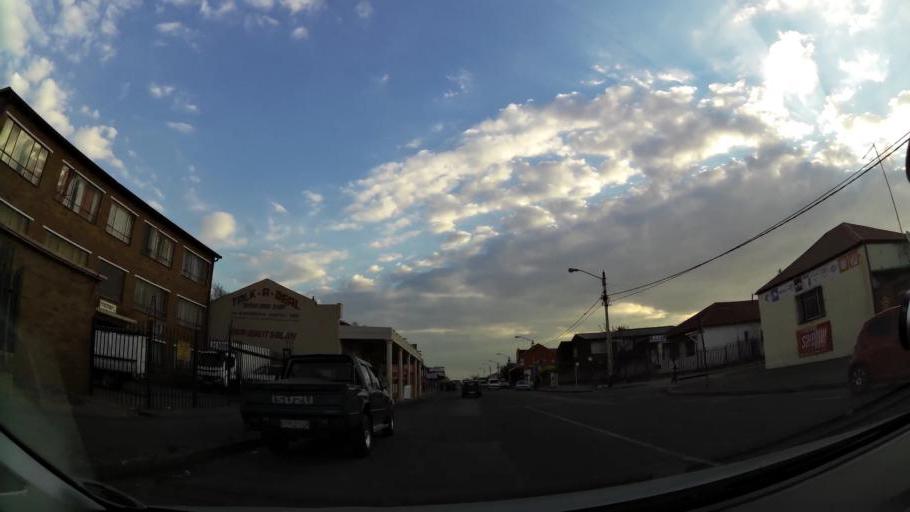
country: ZA
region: Gauteng
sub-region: Ekurhuleni Metropolitan Municipality
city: Germiston
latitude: -26.1868
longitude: 28.1670
